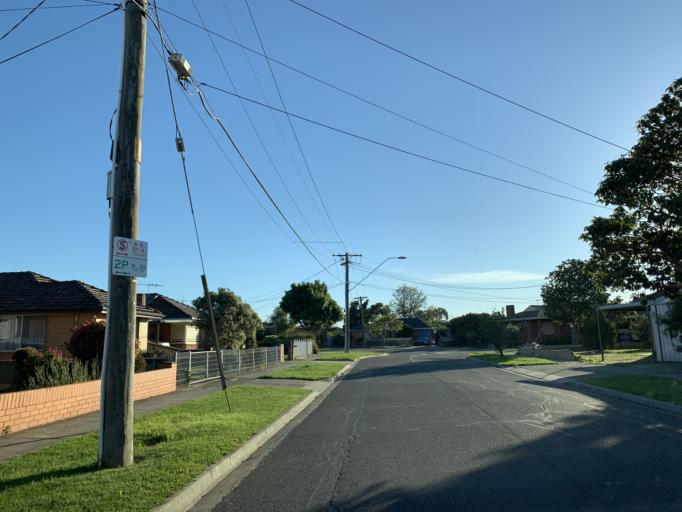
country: AU
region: Victoria
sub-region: Brimbank
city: St Albans
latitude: -37.7547
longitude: 144.8115
